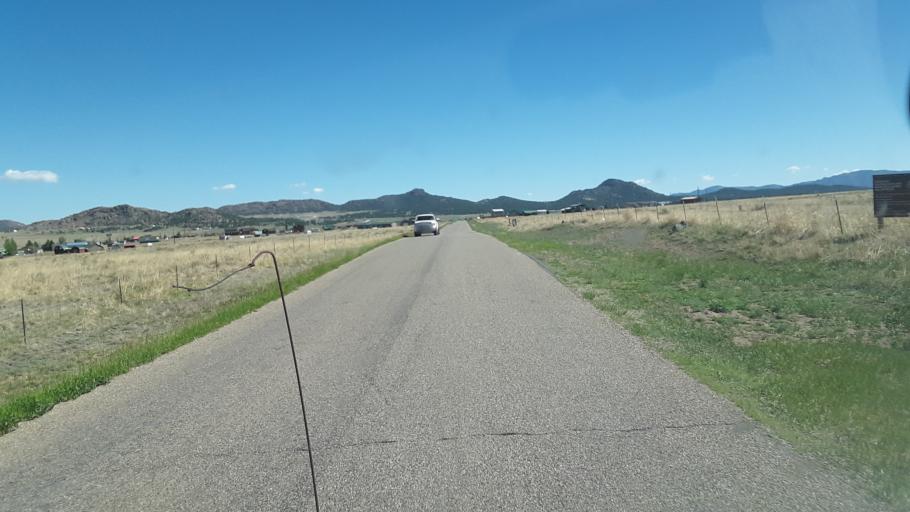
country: US
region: Colorado
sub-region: Custer County
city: Westcliffe
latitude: 38.1891
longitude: -105.4600
